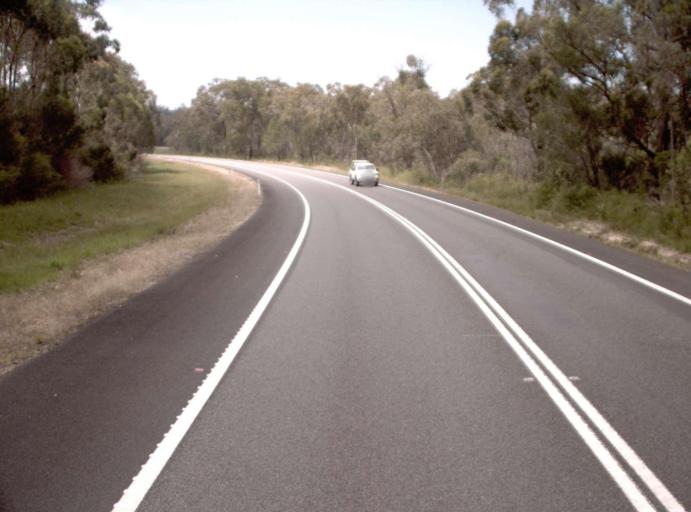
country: AU
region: New South Wales
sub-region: Bega Valley
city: Eden
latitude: -37.5210
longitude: 149.4955
